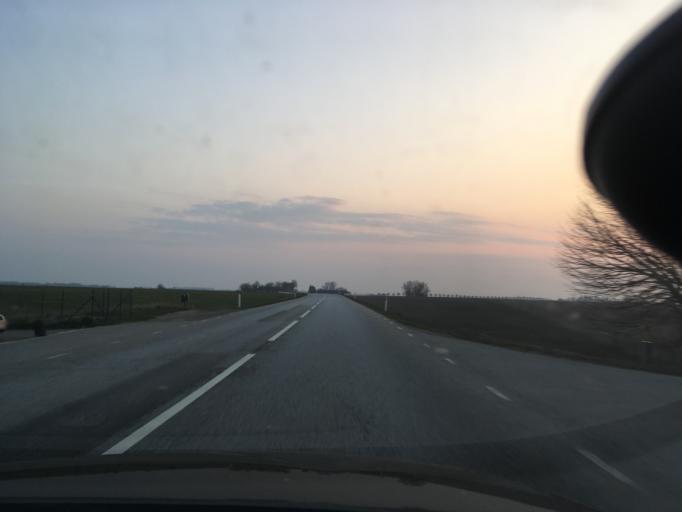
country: SE
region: Skane
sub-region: Ystads Kommun
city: Kopingebro
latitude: 55.4619
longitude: 14.0334
